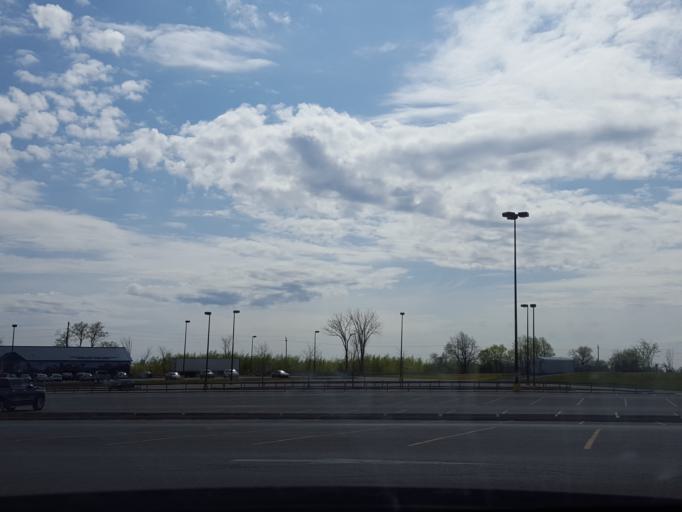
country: CA
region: Ontario
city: Uxbridge
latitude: 44.1798
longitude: -78.8898
